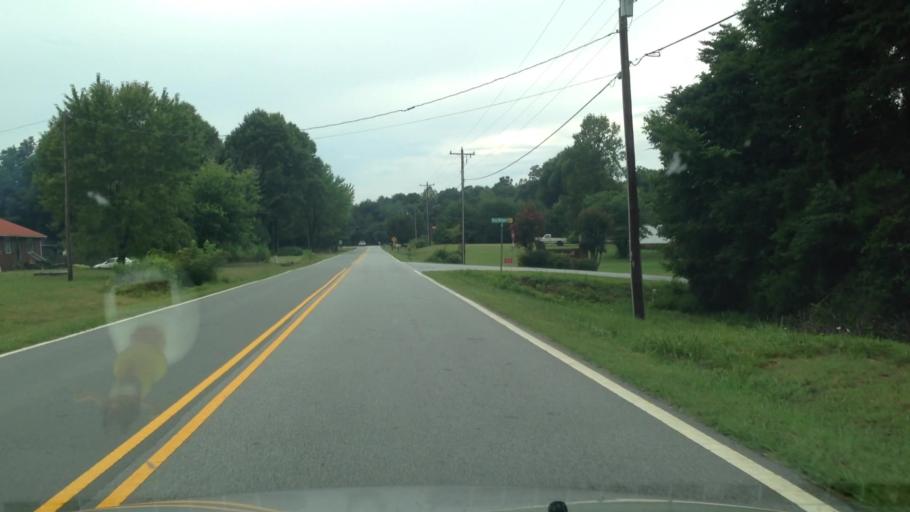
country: US
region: North Carolina
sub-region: Forsyth County
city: Walkertown
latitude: 36.1583
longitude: -80.1196
